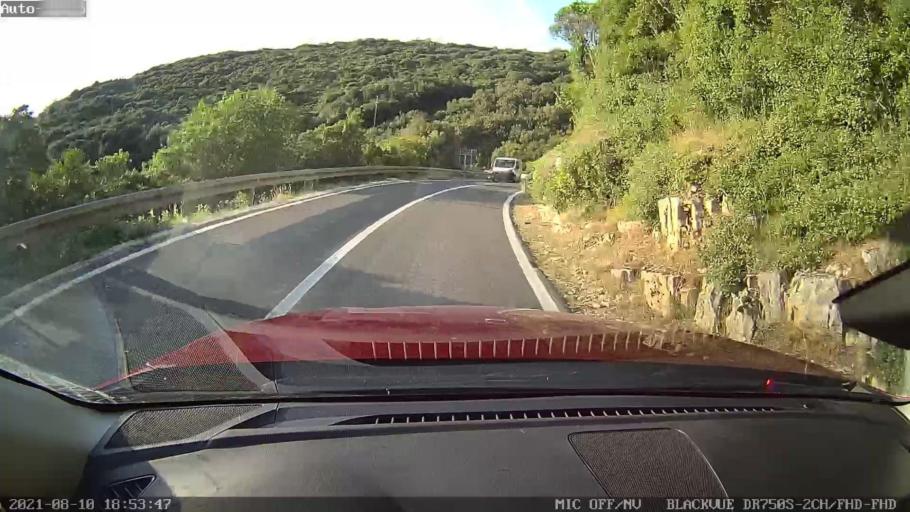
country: HR
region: Istarska
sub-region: Grad Rovinj
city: Rovinj
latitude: 45.1323
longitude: 13.7371
